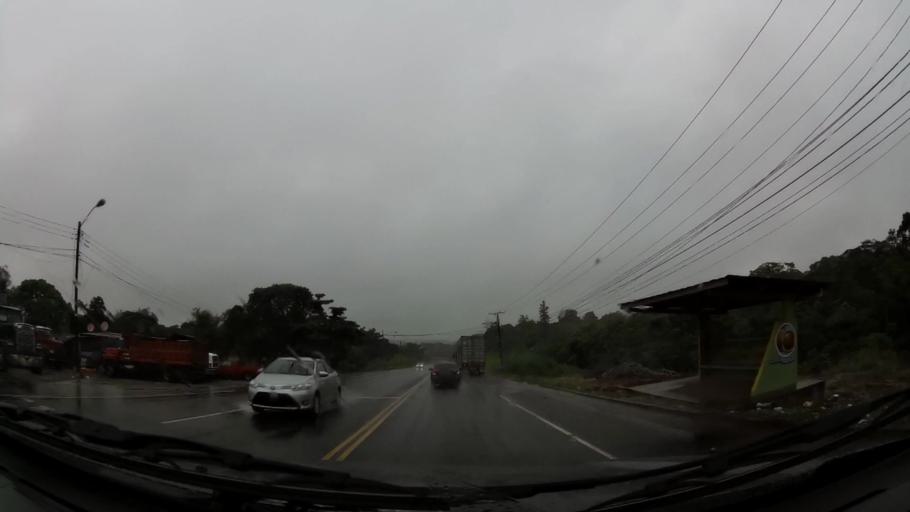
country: PA
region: Colon
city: Santa Rita Arriba
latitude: 9.3178
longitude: -79.7952
